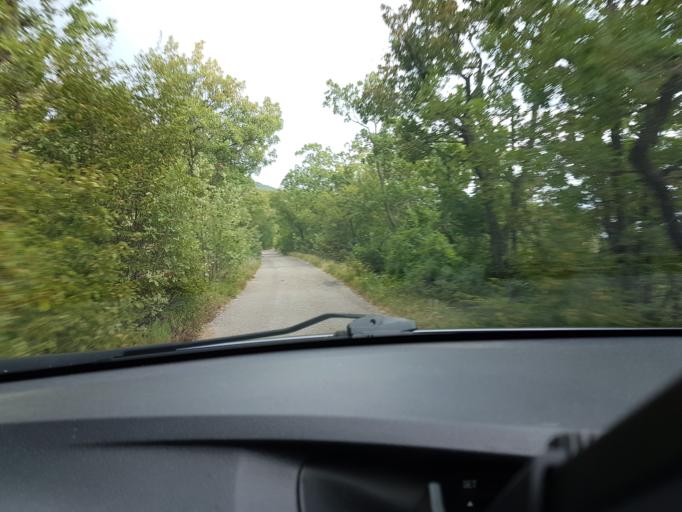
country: HR
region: Primorsko-Goranska
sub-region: Grad Crikvenica
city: Crikvenica
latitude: 45.2297
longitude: 14.7050
